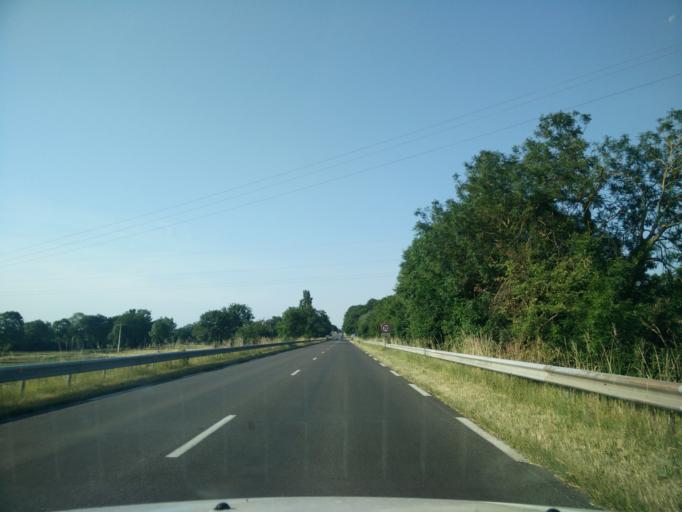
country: FR
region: Auvergne
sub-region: Departement de l'Allier
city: Moulins
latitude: 46.5340
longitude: 3.3190
